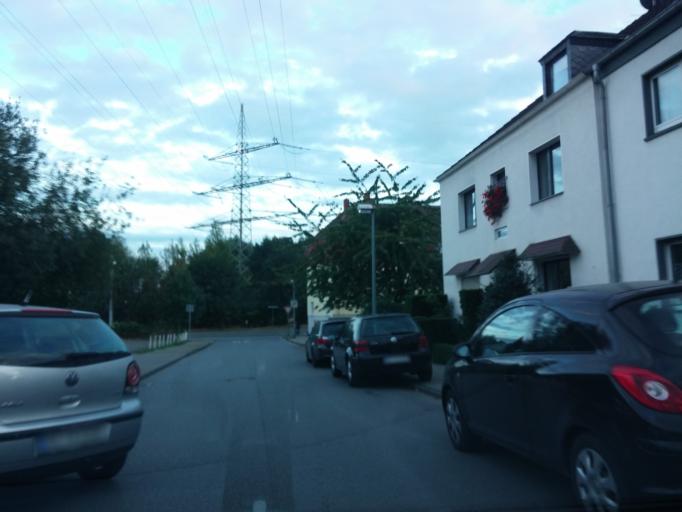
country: DE
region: North Rhine-Westphalia
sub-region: Regierungsbezirk Munster
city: Gladbeck
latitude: 51.5458
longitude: 7.0372
